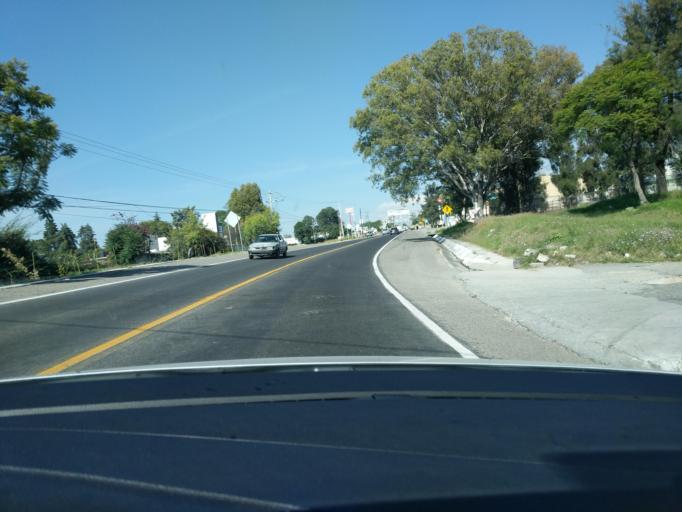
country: MX
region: Puebla
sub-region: Atlixco
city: San Agustin Huixaxtla
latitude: 18.9346
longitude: -98.4045
